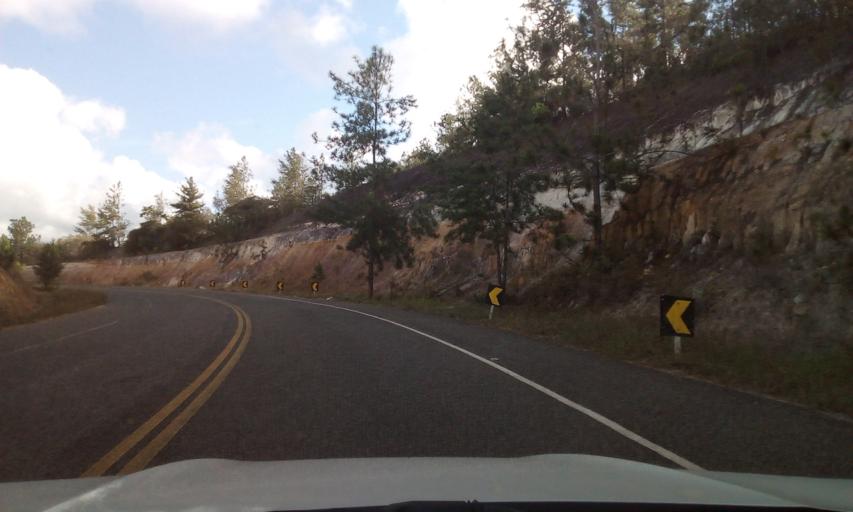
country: BR
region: Bahia
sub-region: Conde
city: Conde
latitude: -12.0960
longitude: -37.7732
